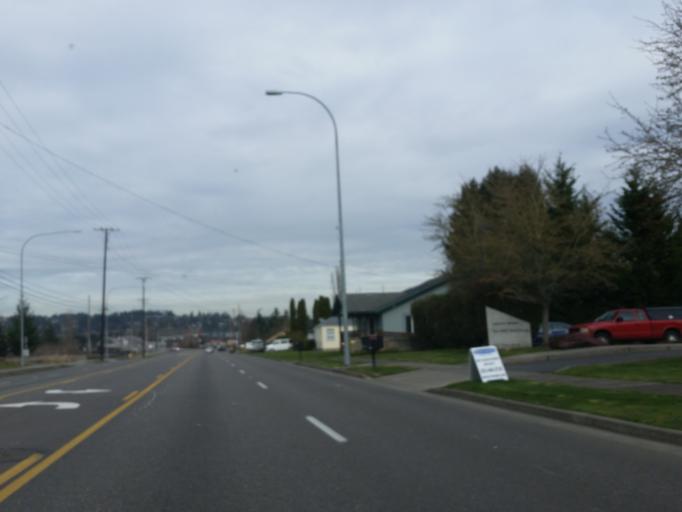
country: US
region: Washington
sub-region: Pierce County
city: Sumner
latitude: 47.1827
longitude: -122.2561
